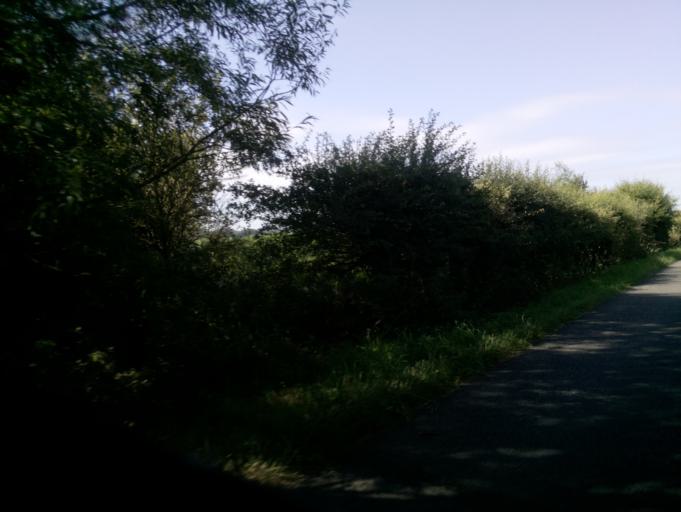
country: GB
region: England
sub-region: Oxfordshire
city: Bampton
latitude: 51.7101
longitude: -1.4991
